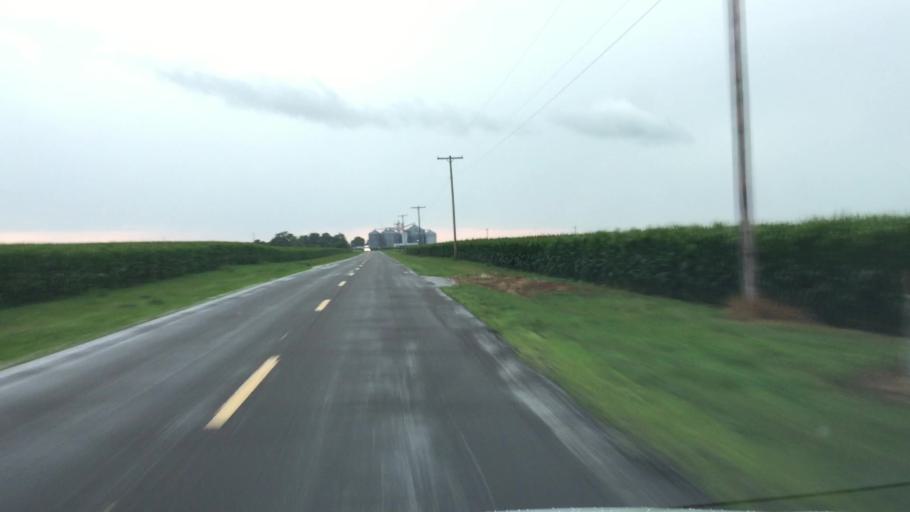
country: US
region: Illinois
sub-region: Hancock County
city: Carthage
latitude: 40.5204
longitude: -91.1521
